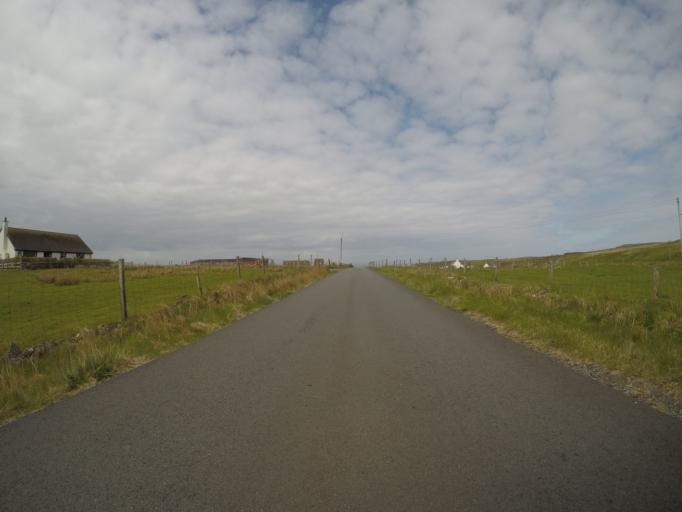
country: GB
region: Scotland
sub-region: Highland
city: Portree
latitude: 57.6450
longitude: -6.3785
